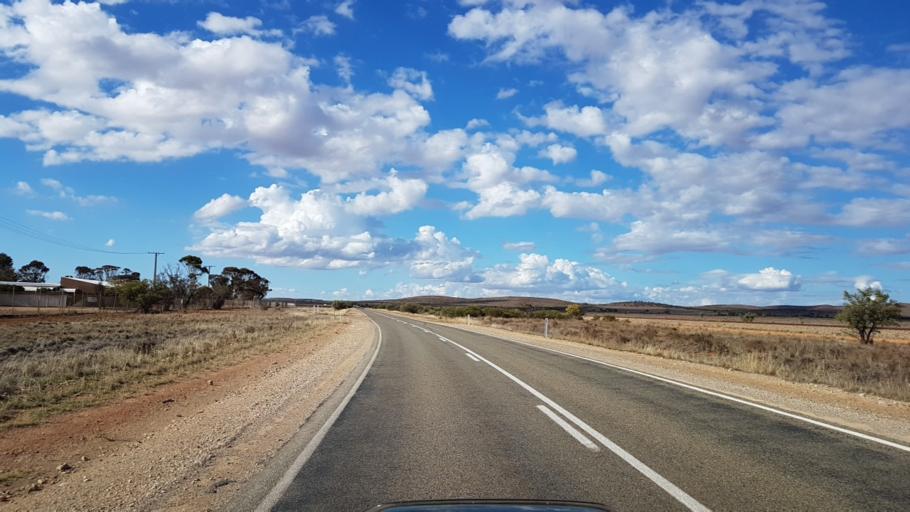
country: AU
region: South Australia
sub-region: Peterborough
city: Peterborough
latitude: -32.9689
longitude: 138.8681
